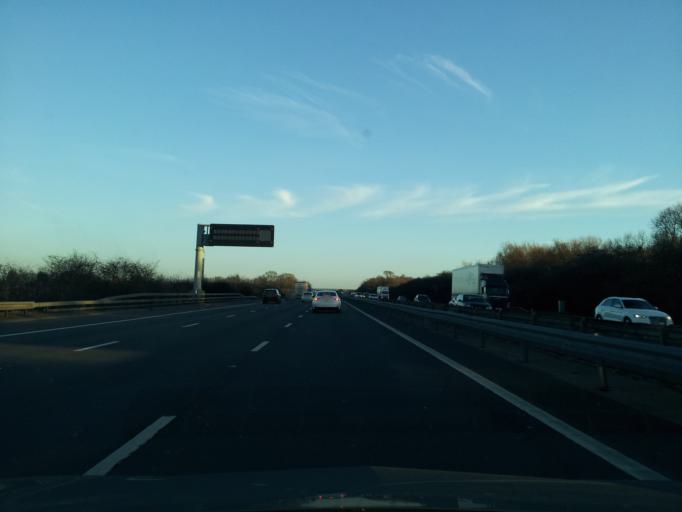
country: GB
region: England
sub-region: Milton Keynes
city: Newport Pagnell
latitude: 52.0709
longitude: -0.7259
